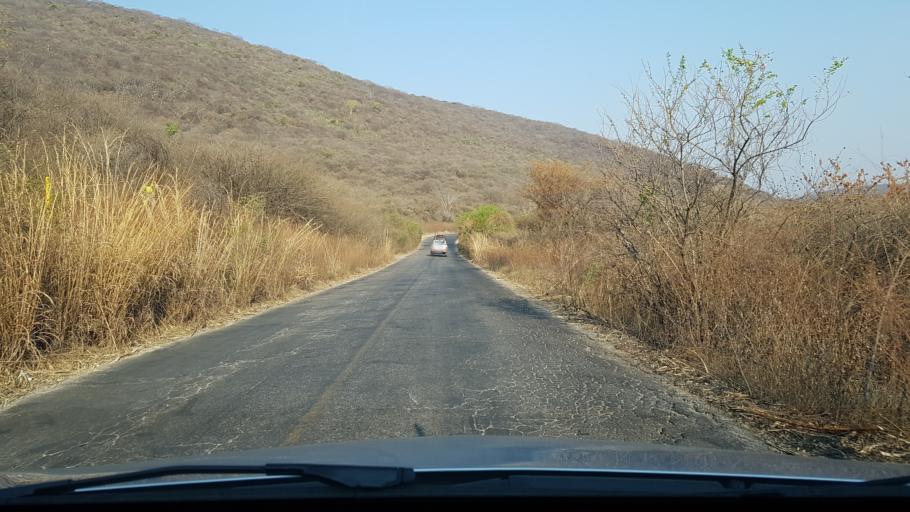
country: MX
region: Morelos
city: Tlaltizapan
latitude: 18.6642
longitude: -99.0498
